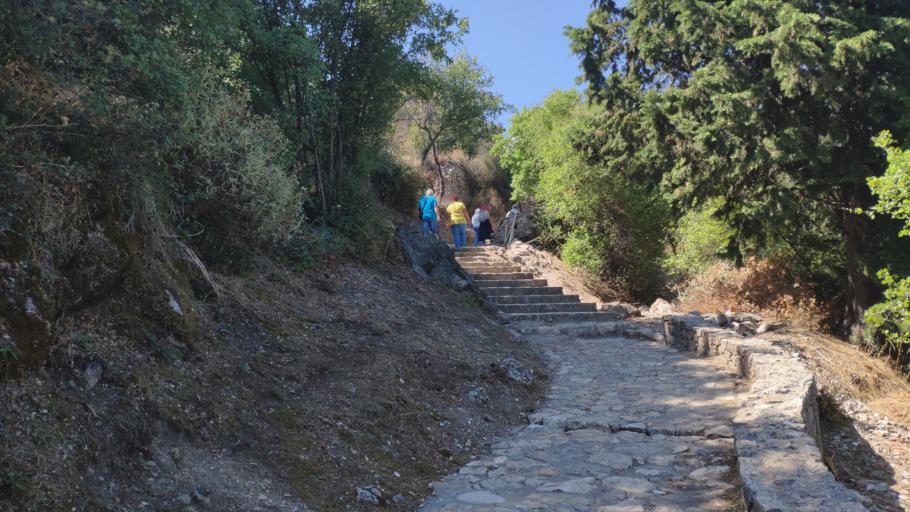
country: GR
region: Peloponnese
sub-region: Nomos Lakonias
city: Magoula
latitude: 37.0731
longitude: 22.3659
